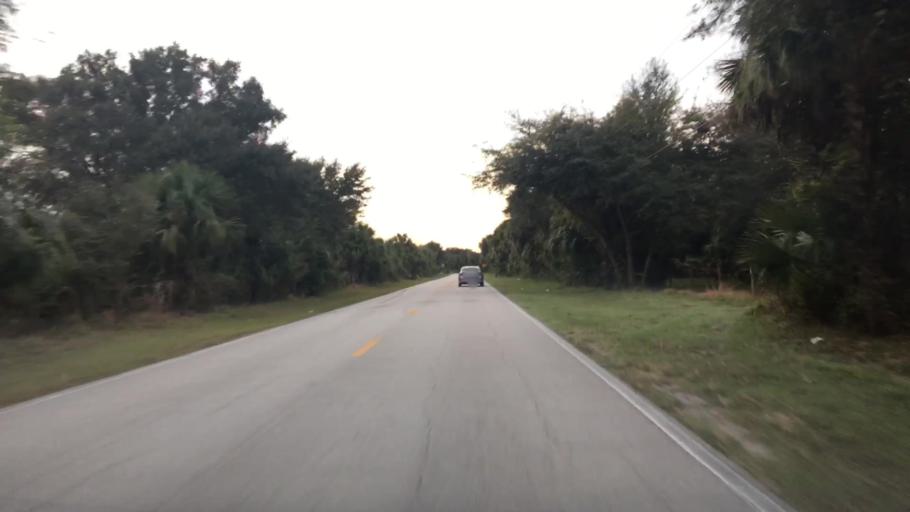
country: US
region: Florida
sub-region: Seminole County
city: Midway
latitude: 28.8237
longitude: -81.1868
